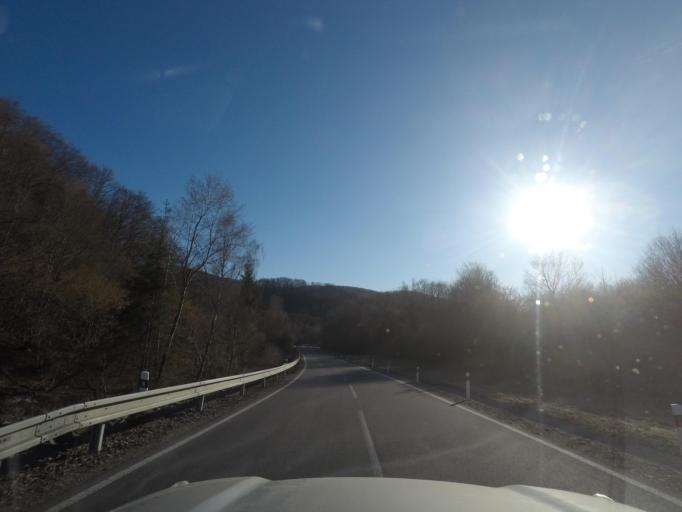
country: SK
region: Presovsky
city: Medzilaborce
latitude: 49.2826
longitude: 21.8446
